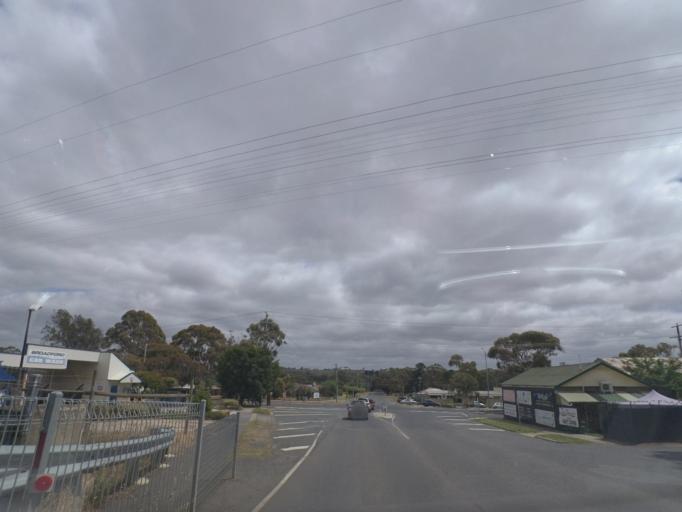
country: AU
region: Victoria
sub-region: Whittlesea
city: Whittlesea
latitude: -37.2060
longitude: 145.0458
